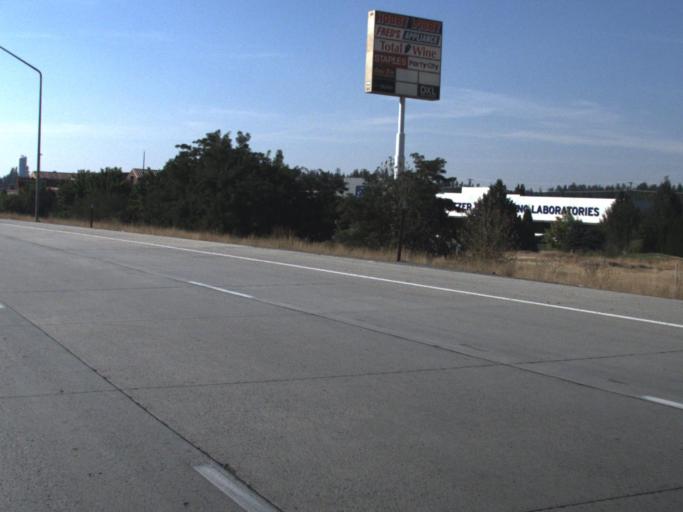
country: US
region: Washington
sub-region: Spokane County
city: Spokane Valley
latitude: 47.6741
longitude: -117.2206
